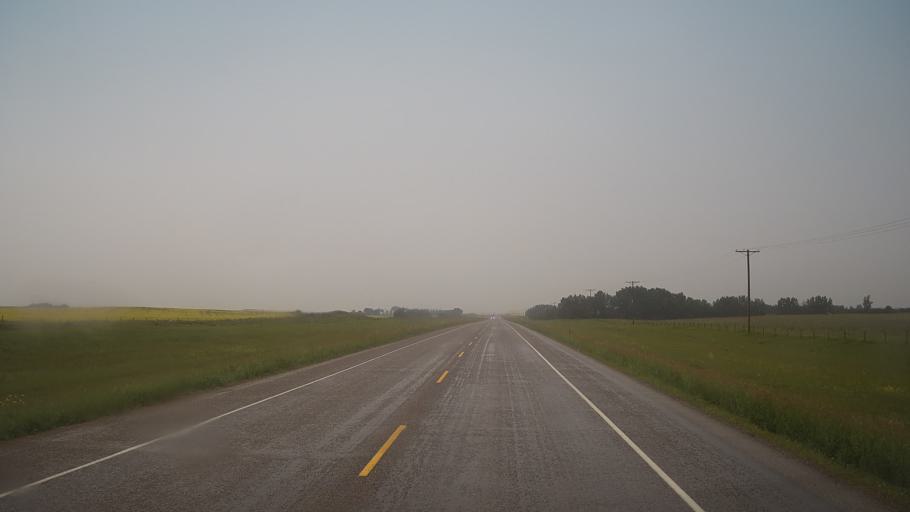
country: CA
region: Saskatchewan
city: Biggar
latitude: 52.1336
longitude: -108.1597
